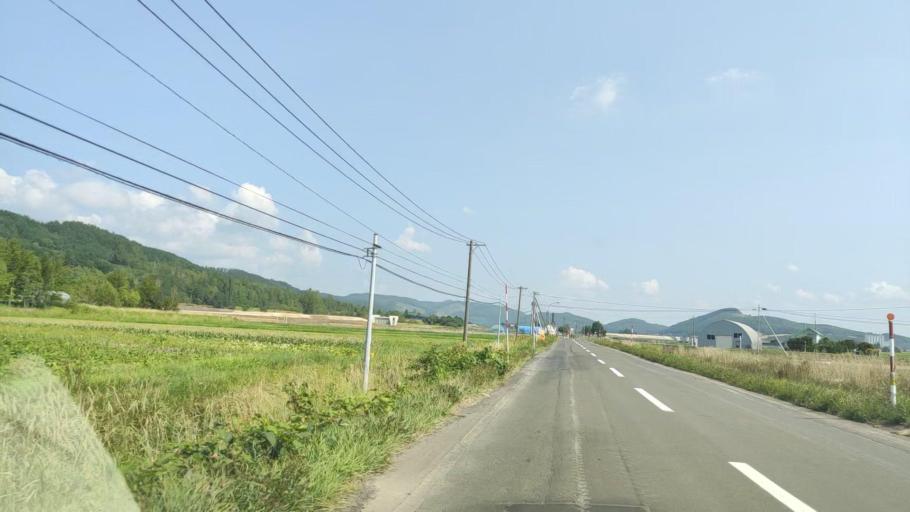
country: JP
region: Hokkaido
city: Shimo-furano
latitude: 43.3801
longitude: 142.3910
